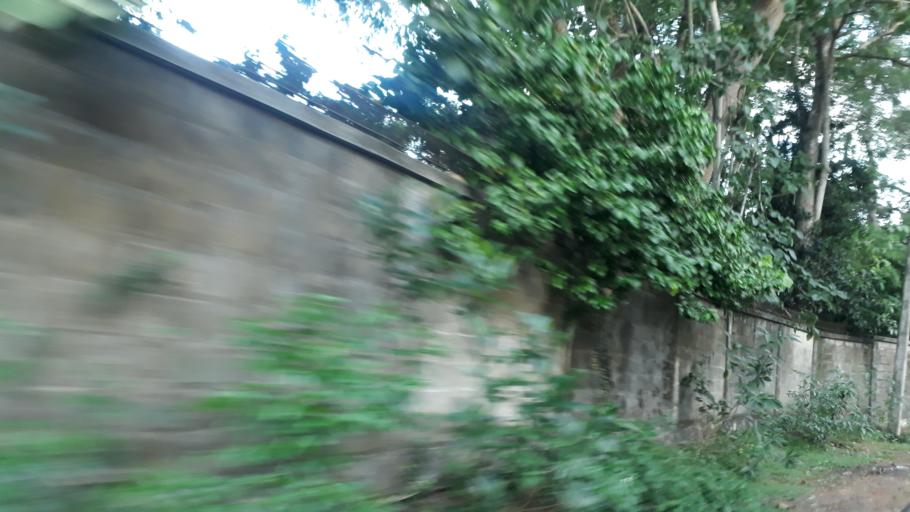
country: LK
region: Western
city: Gampaha
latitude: 7.1014
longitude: 79.9855
